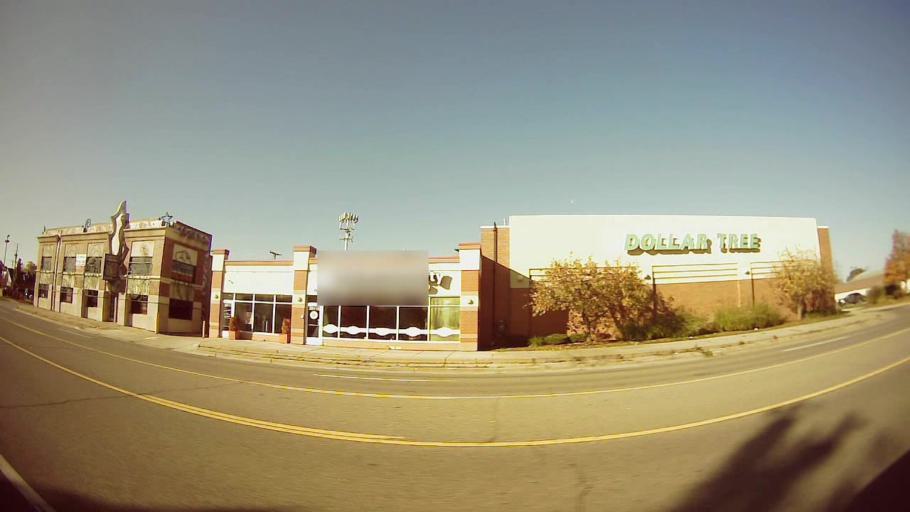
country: US
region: Michigan
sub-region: Oakland County
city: Berkley
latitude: 42.5043
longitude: -83.2031
